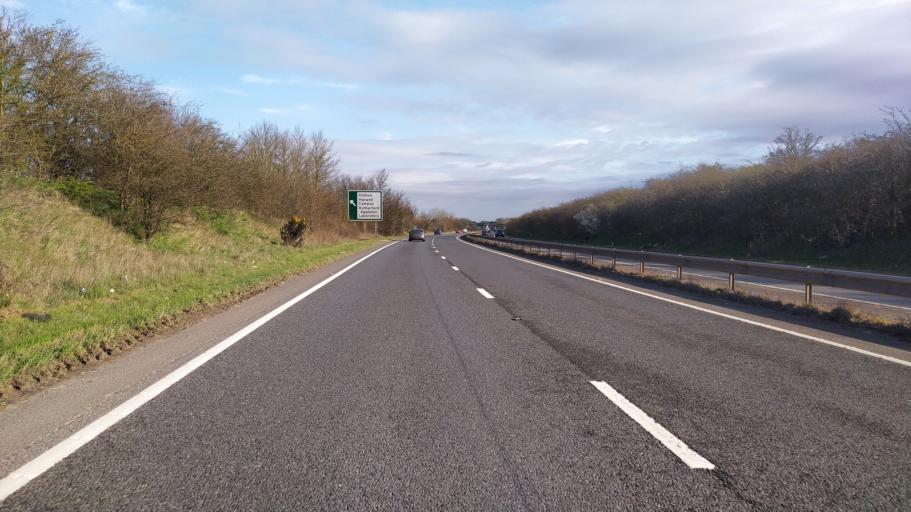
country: GB
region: England
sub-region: Oxfordshire
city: Harwell
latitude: 51.5646
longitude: -1.3019
